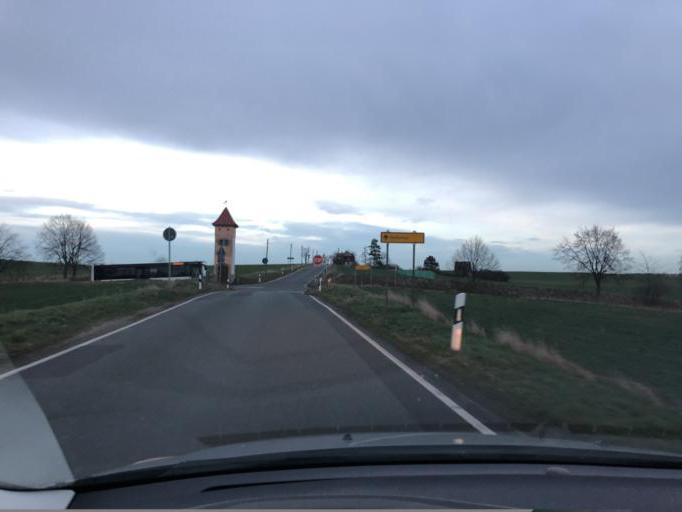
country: DE
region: Saxony-Anhalt
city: Goseck
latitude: 51.2054
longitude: 11.8349
